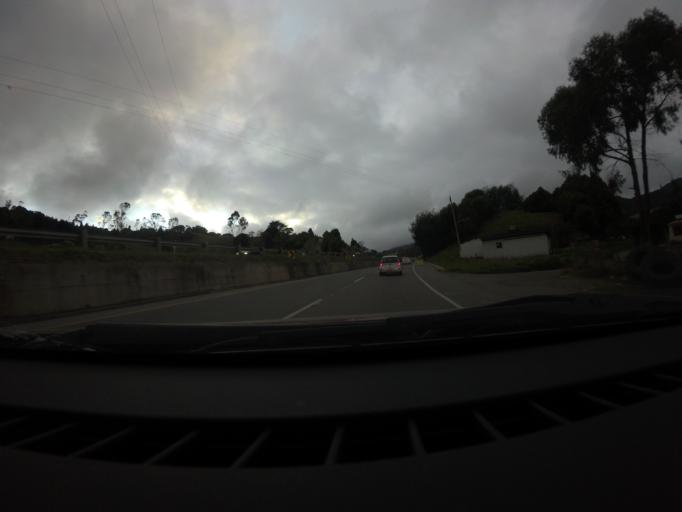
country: CO
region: Boyaca
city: Samaca
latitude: 5.4381
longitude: -73.4439
